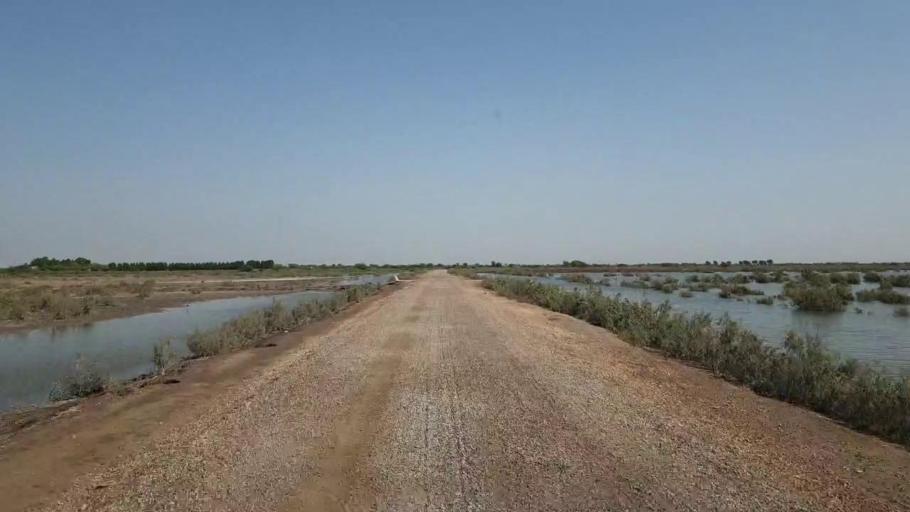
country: PK
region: Sindh
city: Tando Bago
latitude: 24.7302
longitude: 69.0357
